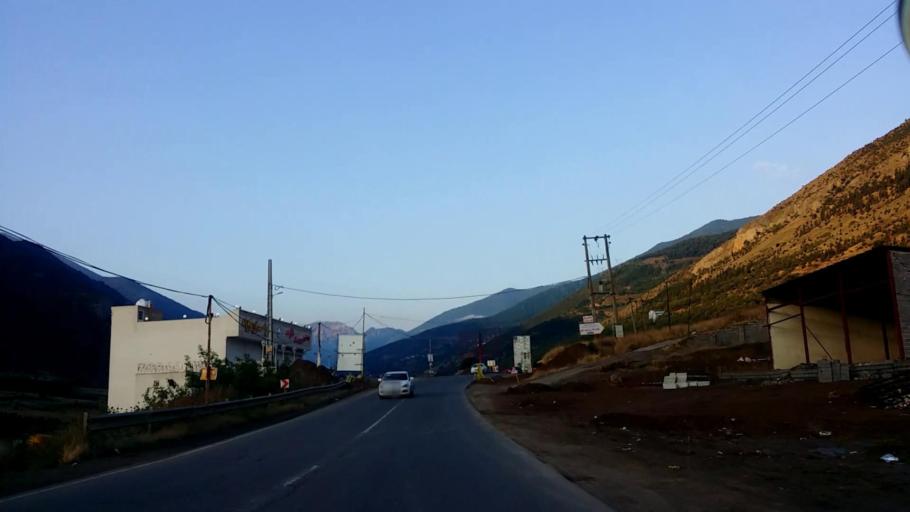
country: IR
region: Mazandaran
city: Chalus
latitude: 36.4383
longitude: 51.2912
